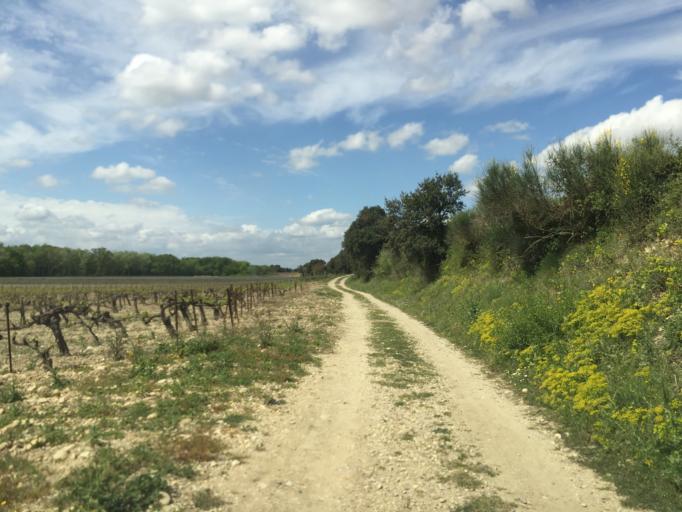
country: FR
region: Provence-Alpes-Cote d'Azur
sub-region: Departement du Vaucluse
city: Chateauneuf-du-Pape
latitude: 44.0450
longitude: 4.8232
